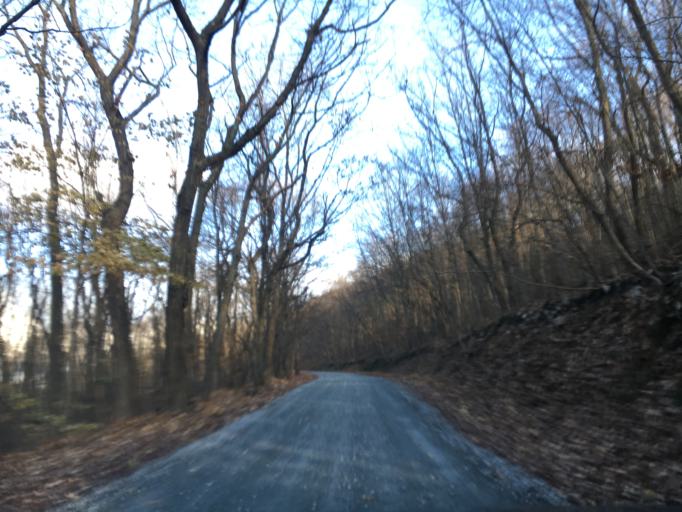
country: US
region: Pennsylvania
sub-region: Carbon County
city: Lehighton
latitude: 40.7691
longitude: -75.7053
